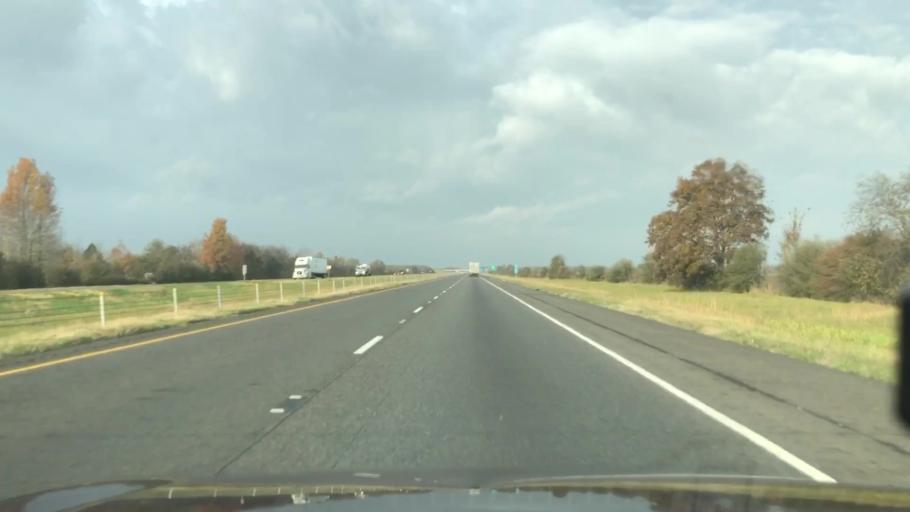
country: US
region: Louisiana
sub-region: Richland Parish
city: Delhi
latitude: 32.4288
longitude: -91.4007
